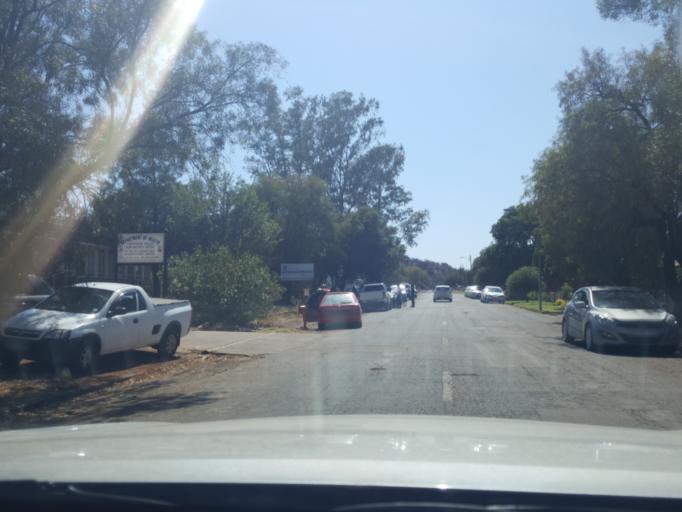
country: ZA
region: North-West
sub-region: Ngaka Modiri Molema District Municipality
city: Zeerust
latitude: -25.5427
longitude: 26.0810
